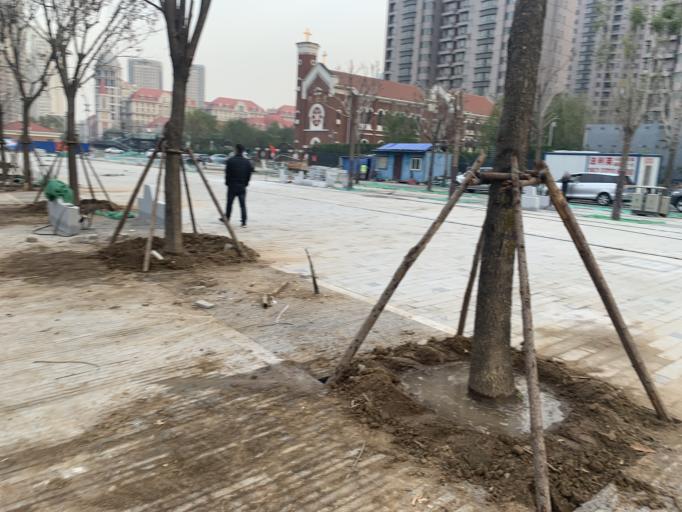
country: CN
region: Tianjin Shi
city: Dahutong
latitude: 39.1403
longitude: 117.1856
